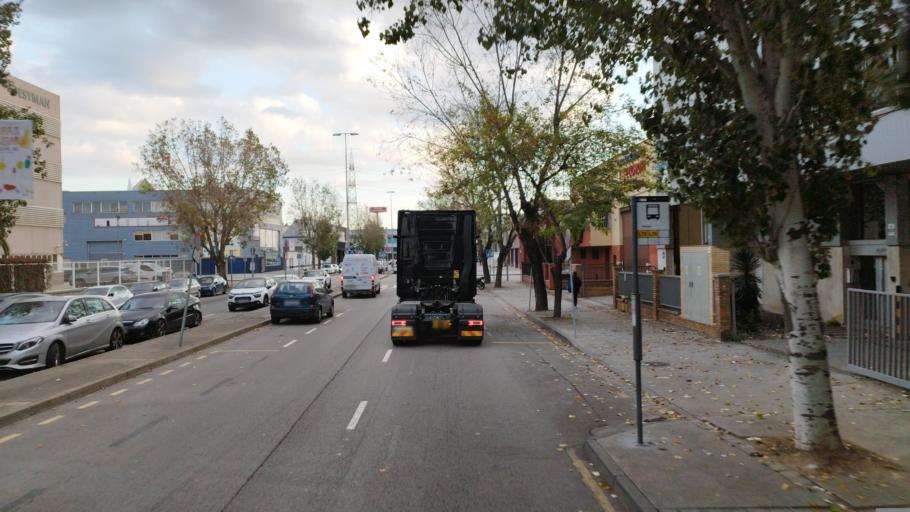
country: ES
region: Catalonia
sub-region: Provincia de Barcelona
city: Sant Boi de Llobregat
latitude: 41.3312
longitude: 2.0444
